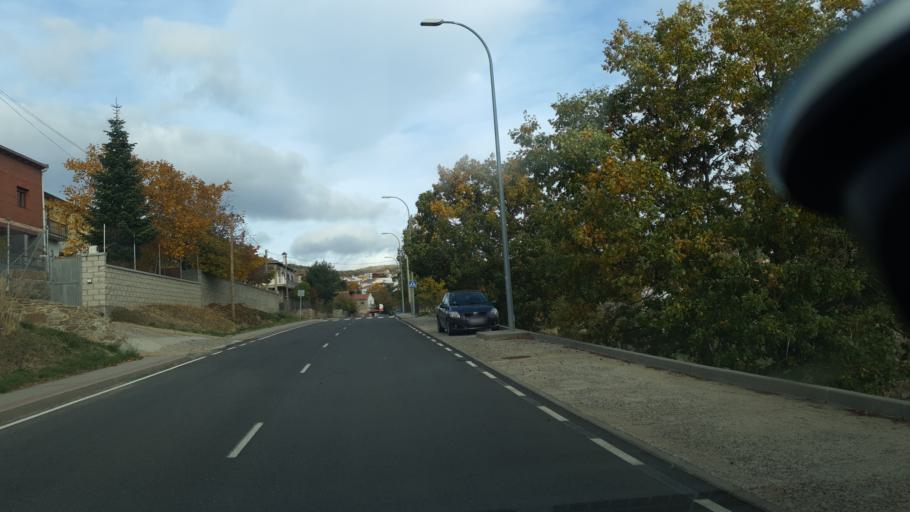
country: ES
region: Castille and Leon
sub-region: Provincia de Avila
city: Navalosa
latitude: 40.3991
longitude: -4.9349
